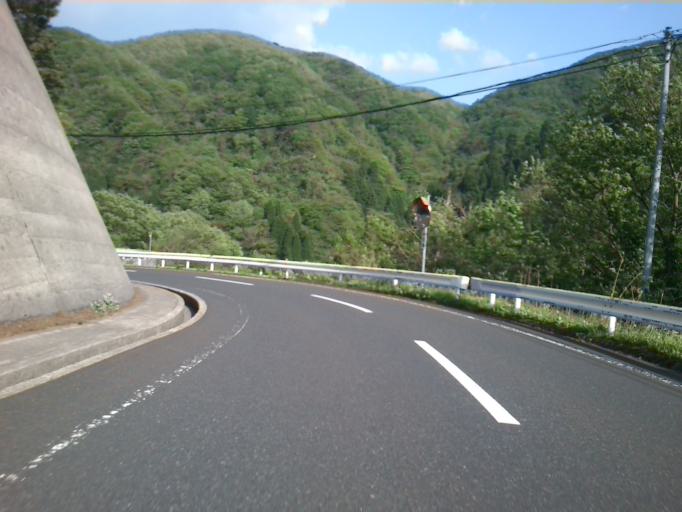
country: JP
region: Kyoto
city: Miyazu
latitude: 35.7010
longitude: 135.1831
